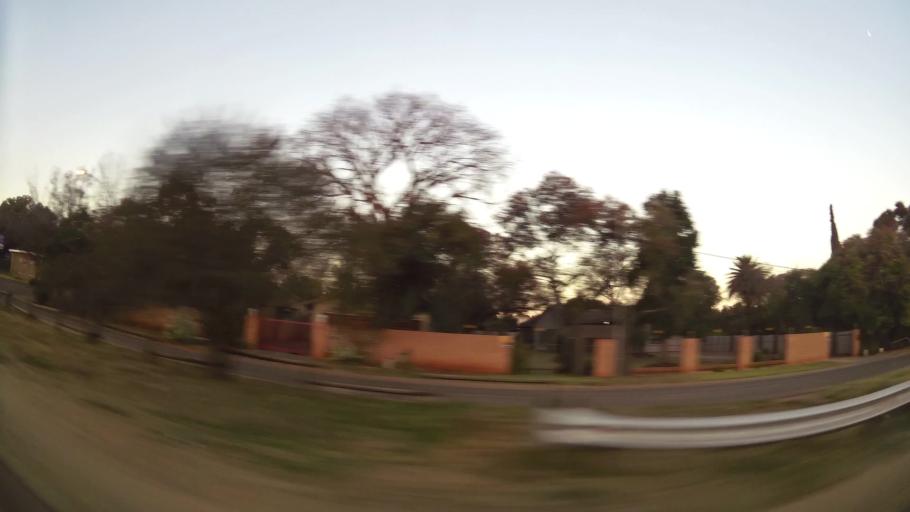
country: ZA
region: Gauteng
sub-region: City of Tshwane Metropolitan Municipality
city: Centurion
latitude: -25.8450
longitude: 28.1531
